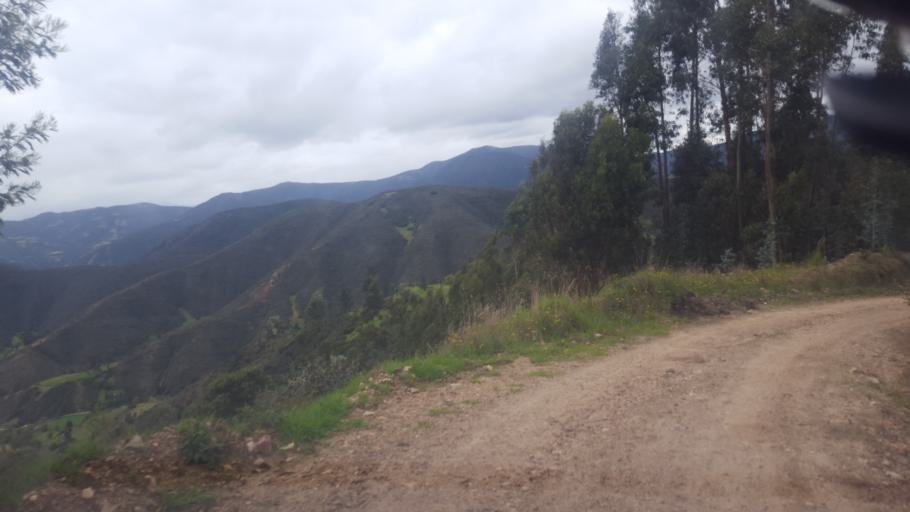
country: CO
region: Boyaca
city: Belen
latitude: 6.0246
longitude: -72.8776
